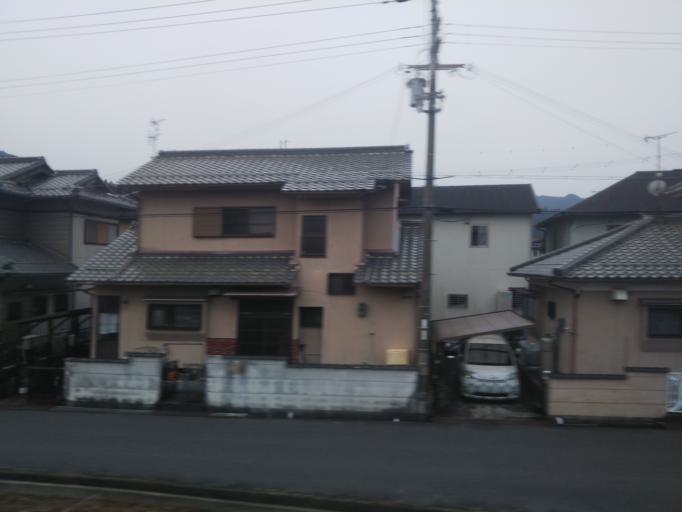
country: JP
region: Shiga Prefecture
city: Minakuchicho-matoba
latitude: 34.9849
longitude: 136.1106
